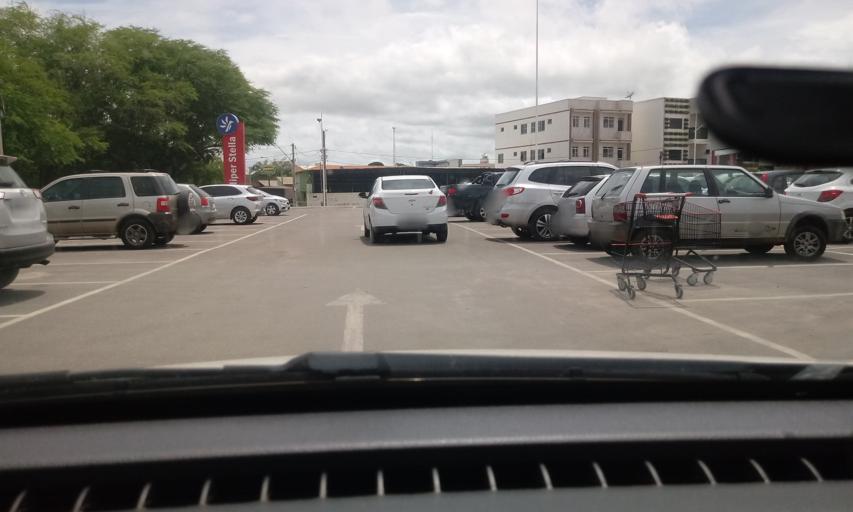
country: BR
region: Bahia
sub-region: Guanambi
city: Guanambi
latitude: -14.2272
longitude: -42.7768
